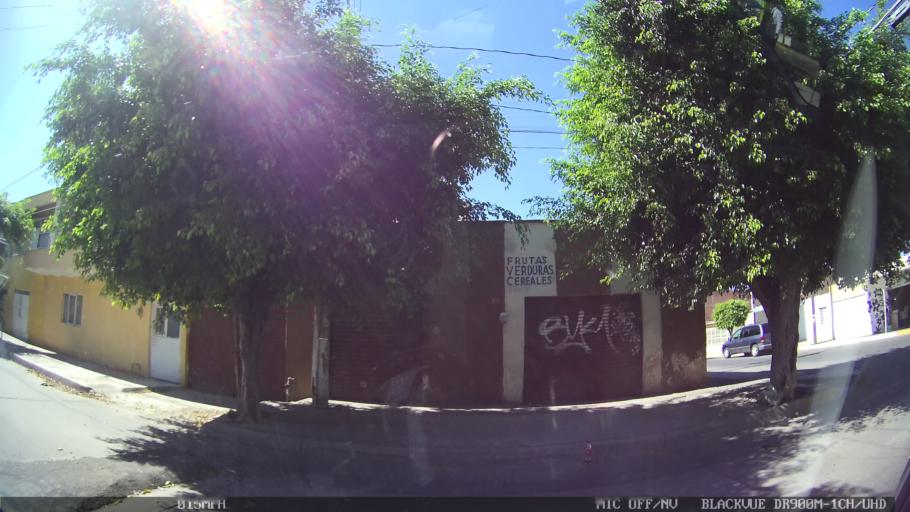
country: MX
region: Jalisco
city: Tlaquepaque
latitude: 20.6565
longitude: -103.2877
